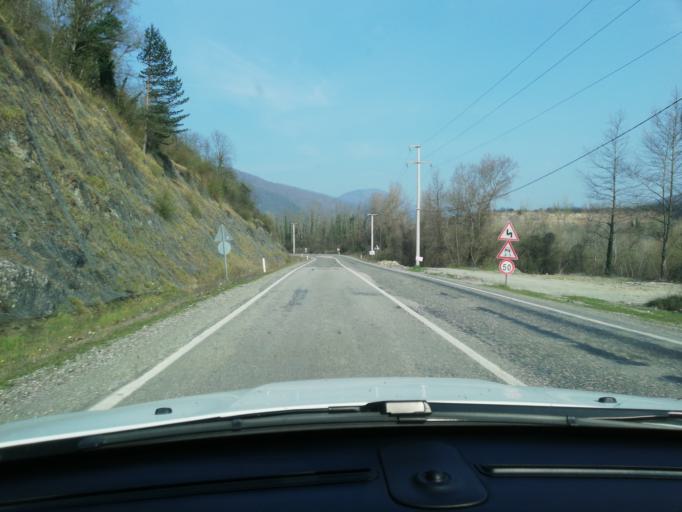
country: TR
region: Karabuk
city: Yenice
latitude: 41.2026
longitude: 32.3726
